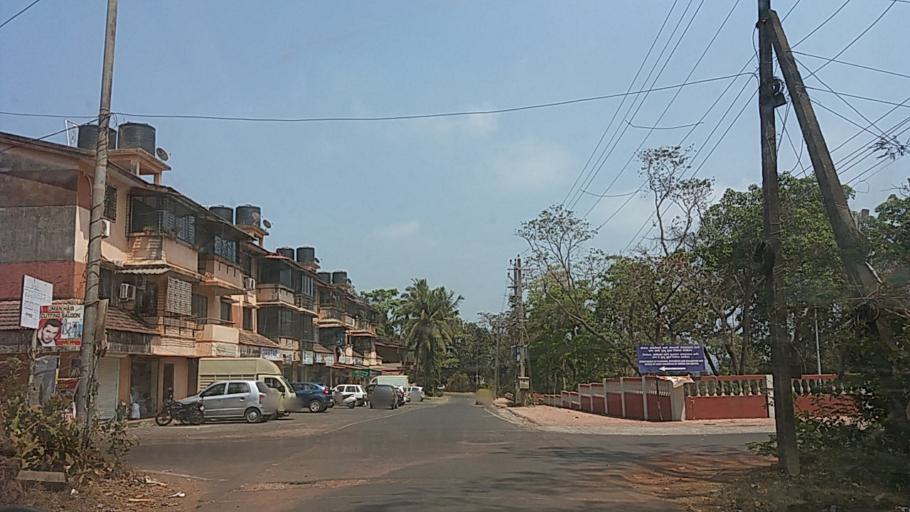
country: IN
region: Goa
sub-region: North Goa
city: Panaji
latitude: 15.5157
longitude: 73.8372
